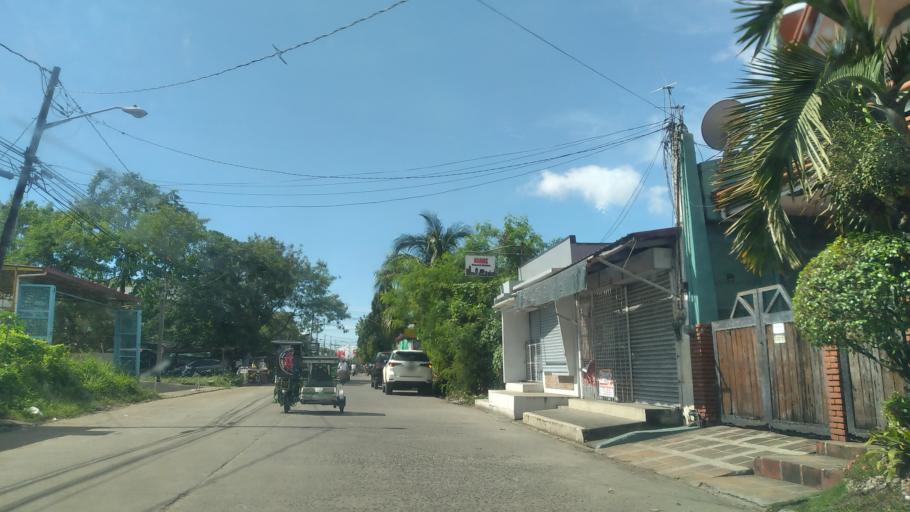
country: PH
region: Calabarzon
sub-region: Province of Quezon
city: Lucena
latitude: 13.9421
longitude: 121.6045
